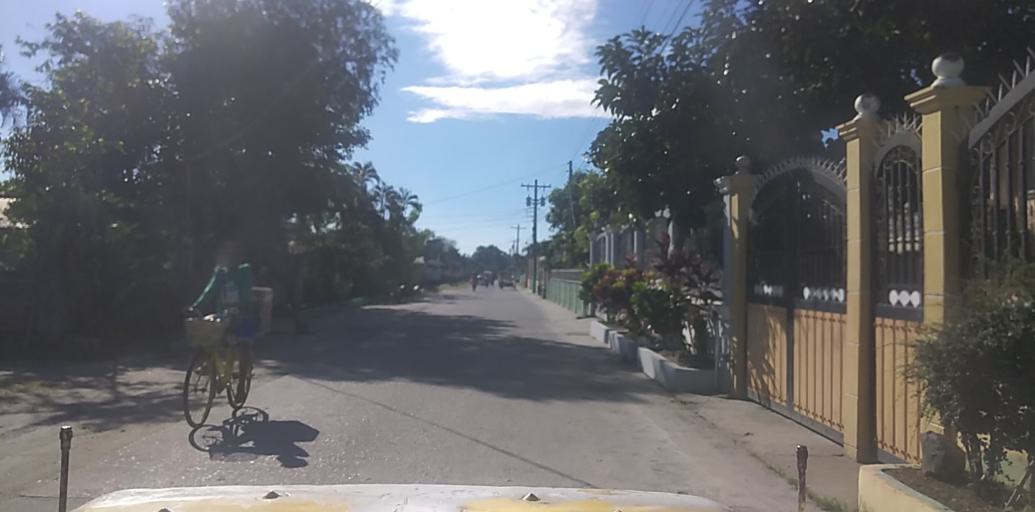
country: PH
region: Central Luzon
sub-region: Province of Pampanga
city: San Patricio
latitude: 15.1089
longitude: 120.7123
